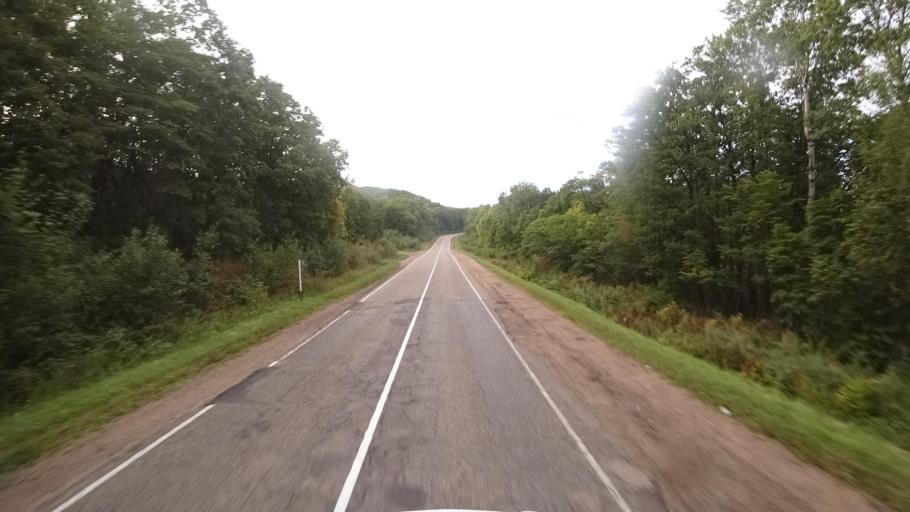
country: RU
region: Primorskiy
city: Yakovlevka
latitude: 44.4003
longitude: 133.4658
